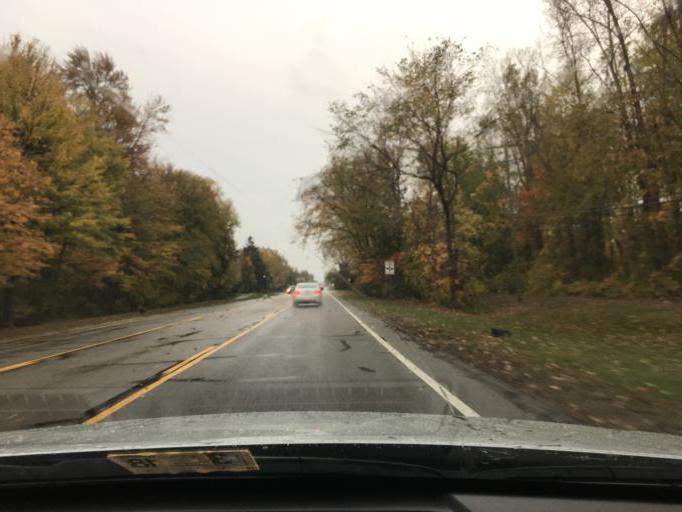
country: US
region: Michigan
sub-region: Oakland County
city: Rochester Hills
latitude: 42.6468
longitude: -83.1122
